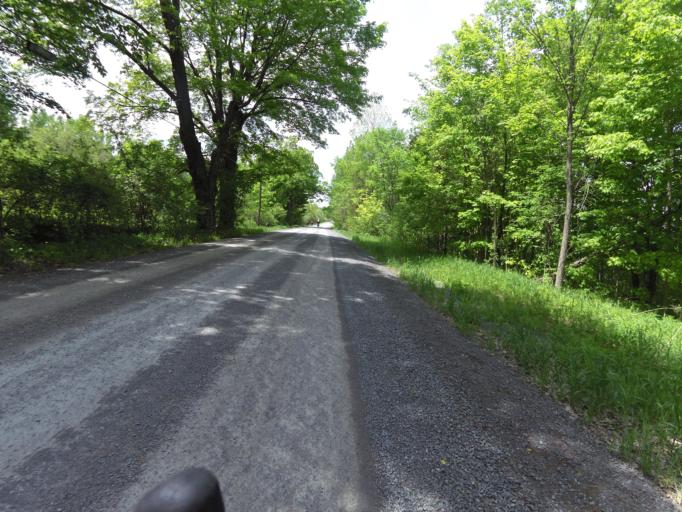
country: CA
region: Ontario
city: Ottawa
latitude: 45.3934
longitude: -75.5344
